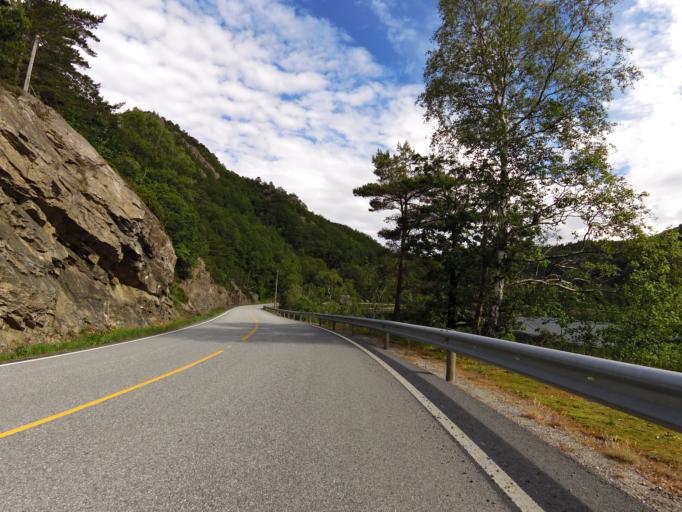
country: NO
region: Vest-Agder
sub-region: Lindesnes
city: Vigeland
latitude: 58.0555
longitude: 7.1773
